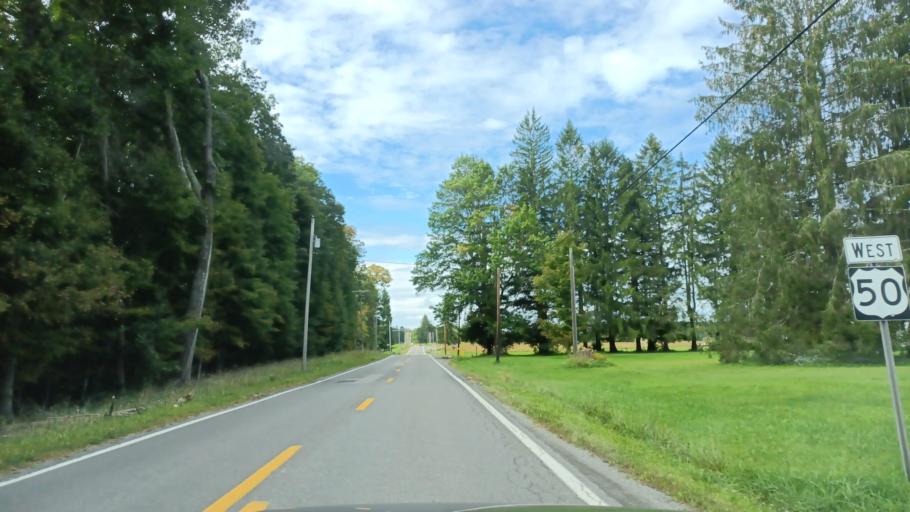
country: US
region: West Virginia
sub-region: Preston County
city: Terra Alta
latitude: 39.3171
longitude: -79.5714
